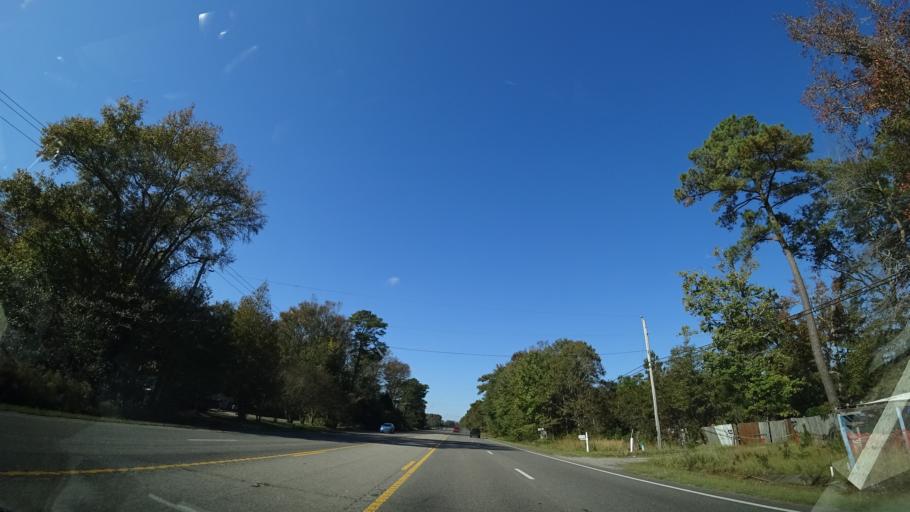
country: US
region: North Carolina
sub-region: Dare County
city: Southern Shores
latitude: 36.2601
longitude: -75.8984
